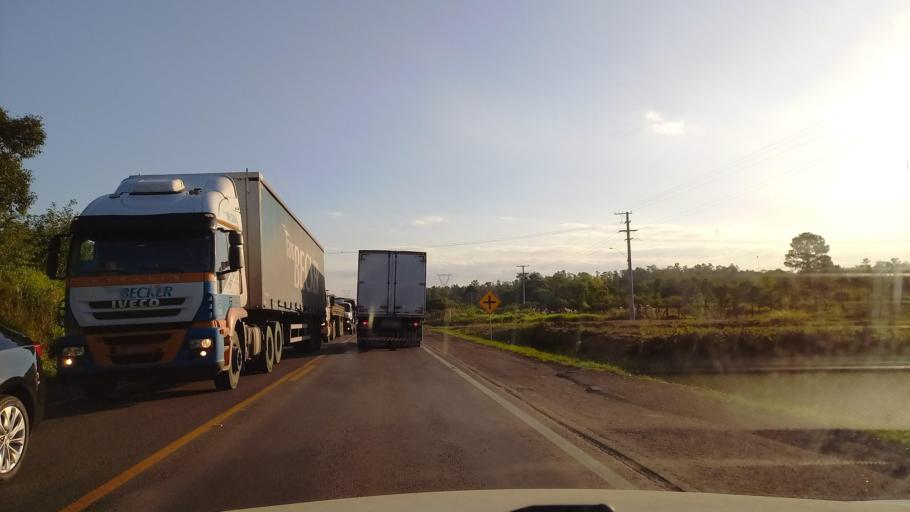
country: BR
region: Rio Grande do Sul
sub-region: Venancio Aires
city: Venancio Aires
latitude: -29.6394
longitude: -52.1615
